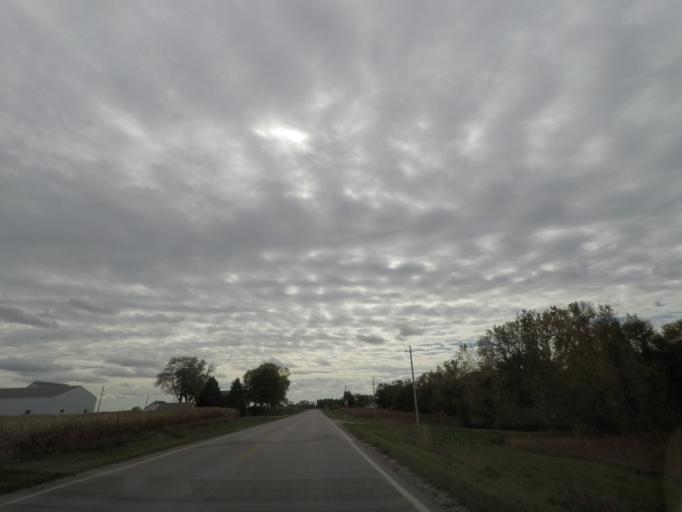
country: US
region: Iowa
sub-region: Story County
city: Huxley
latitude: 41.8442
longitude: -93.5316
